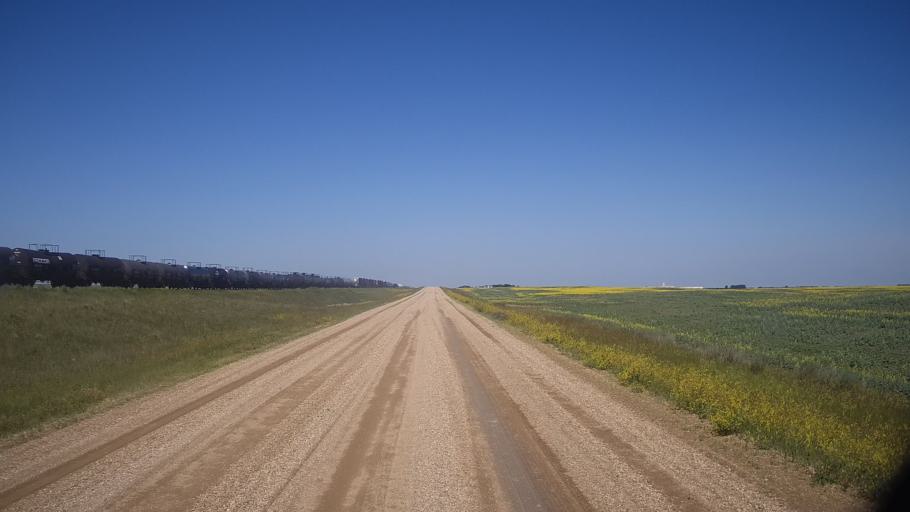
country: CA
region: Saskatchewan
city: Watrous
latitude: 51.8567
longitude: -105.9521
